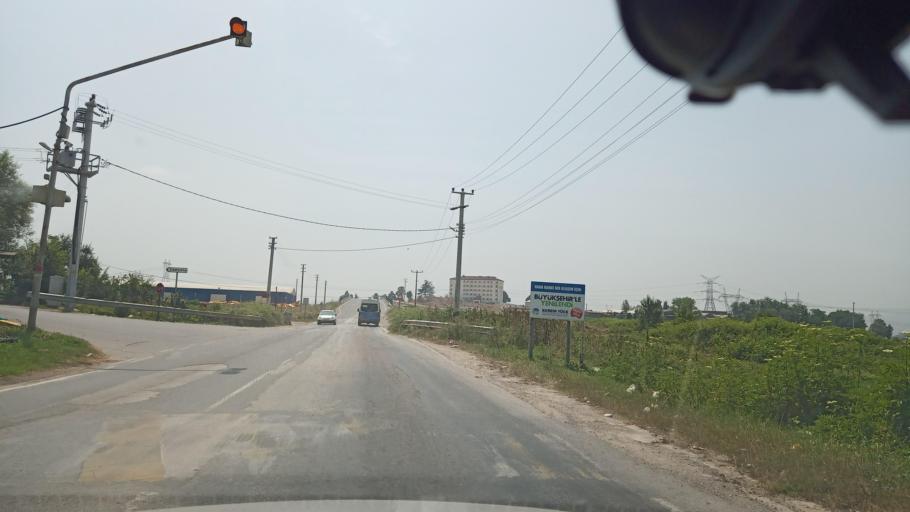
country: TR
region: Sakarya
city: Adapazari
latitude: 40.8275
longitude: 30.3965
